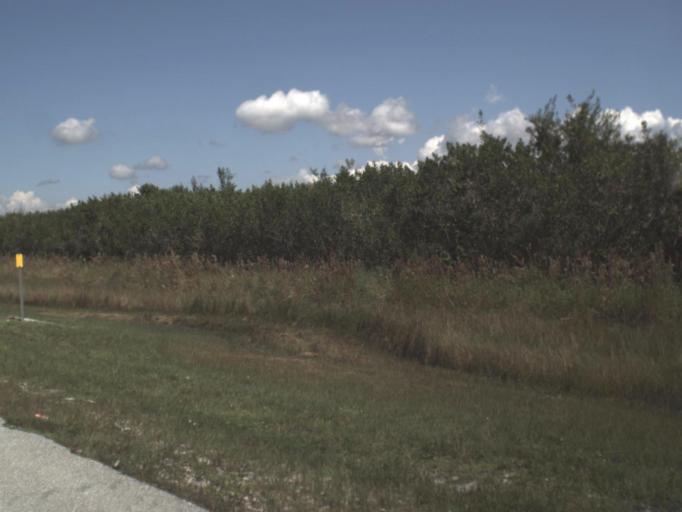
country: US
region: Florida
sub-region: Lee County
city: Pine Island Center
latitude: 26.6187
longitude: -82.0406
